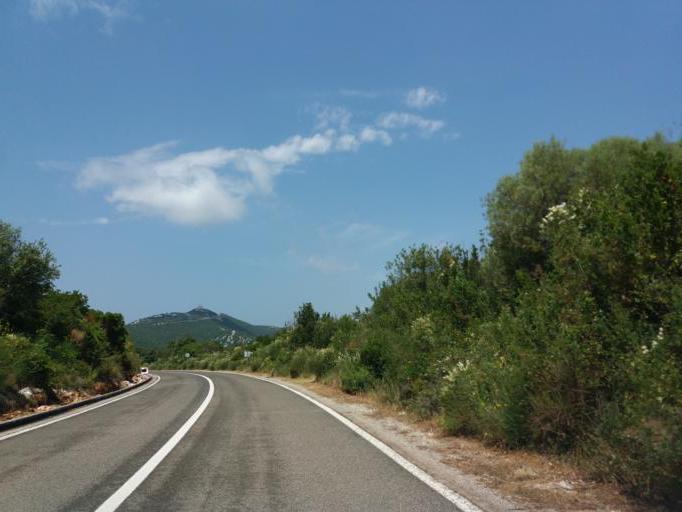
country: HR
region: Zadarska
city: Sali
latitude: 43.9795
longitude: 15.0826
